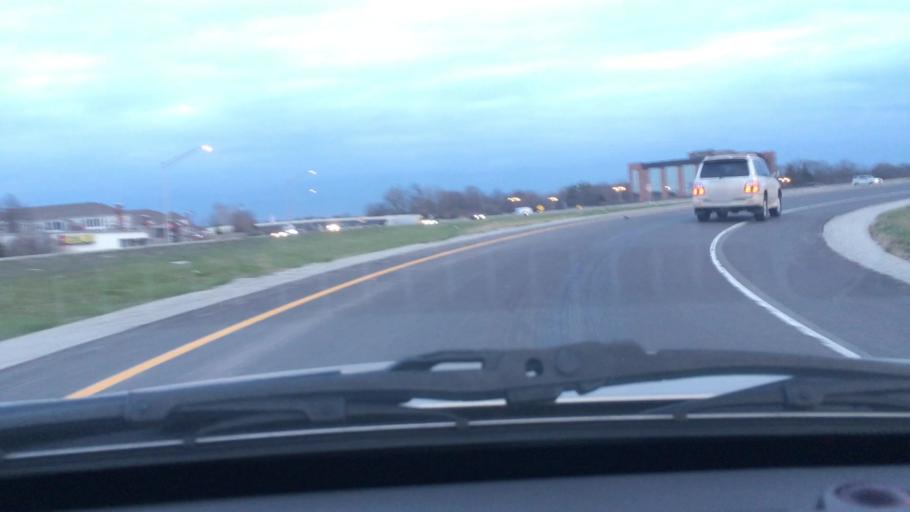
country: US
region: Indiana
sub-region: Marion County
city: Lawrence
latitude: 39.8953
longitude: -86.0521
